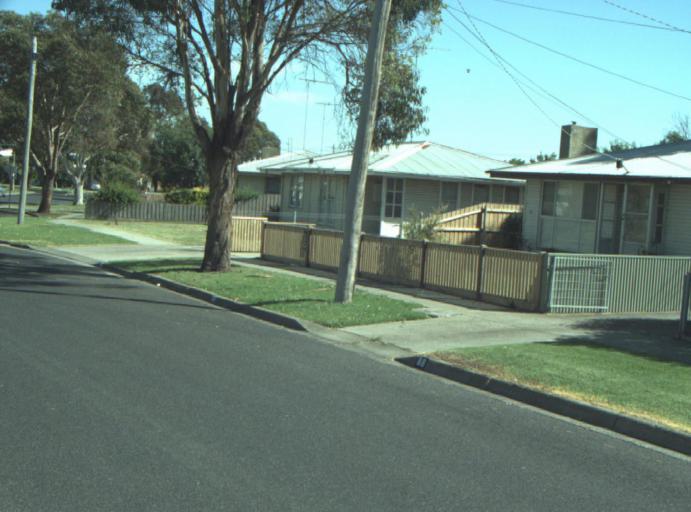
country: AU
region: Victoria
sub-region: Greater Geelong
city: Bell Park
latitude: -38.0853
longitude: 144.3507
